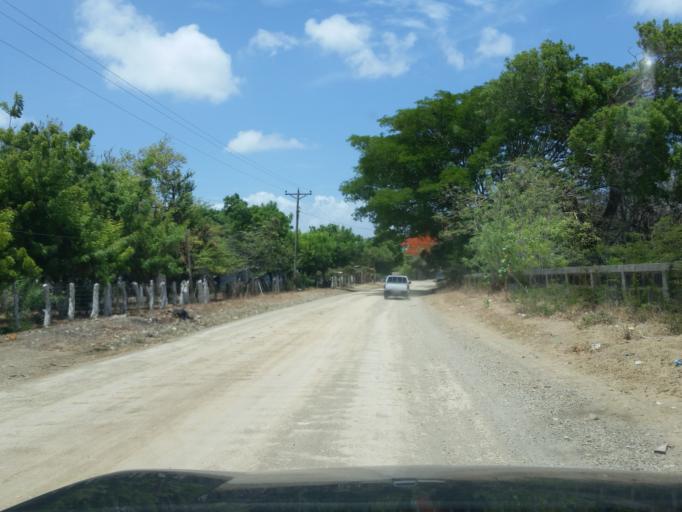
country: NI
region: Rivas
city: Tola
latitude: 11.4628
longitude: -86.0821
